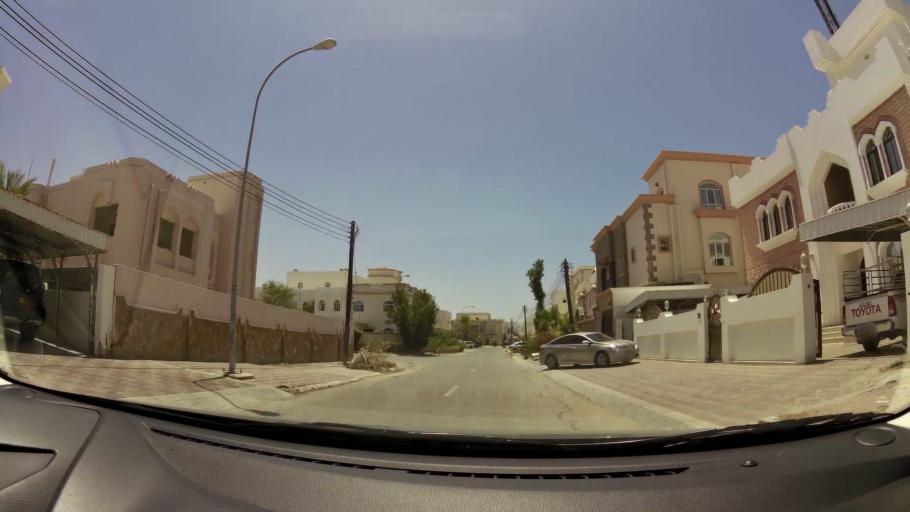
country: OM
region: Muhafazat Masqat
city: Bawshar
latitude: 23.5993
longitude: 58.3791
